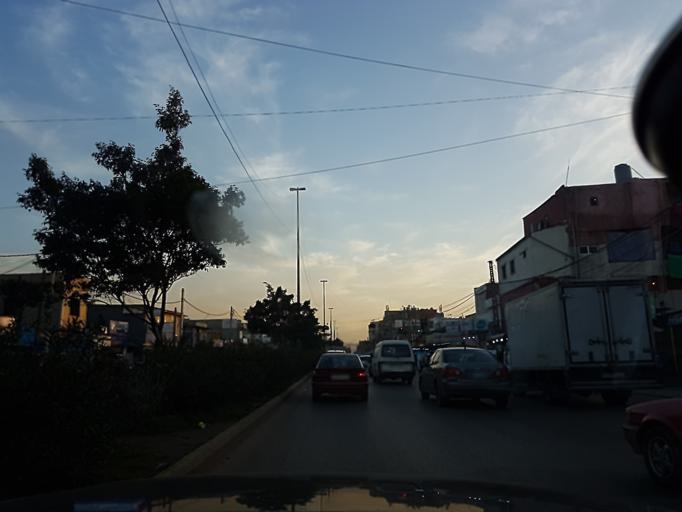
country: LB
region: Beyrouth
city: Beirut
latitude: 33.8380
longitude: 35.4846
